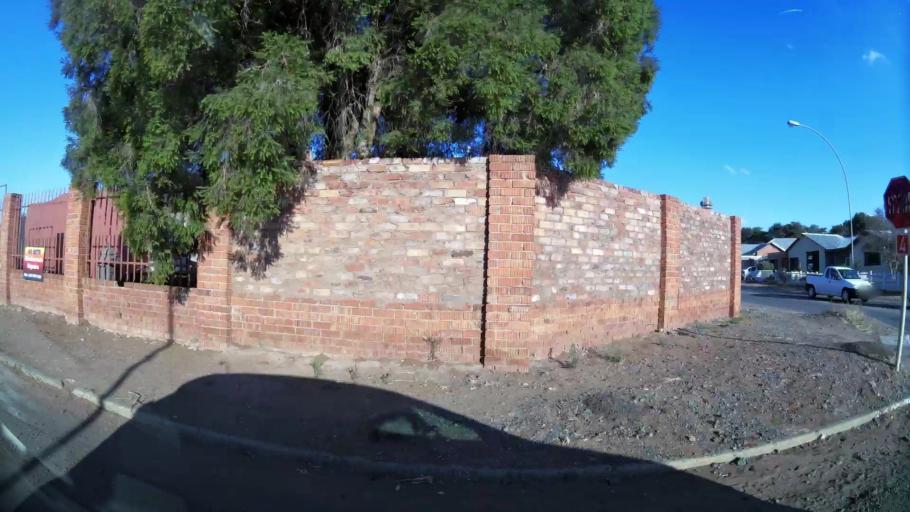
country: ZA
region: Northern Cape
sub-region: Frances Baard District Municipality
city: Kimberley
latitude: -28.7380
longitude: 24.7486
